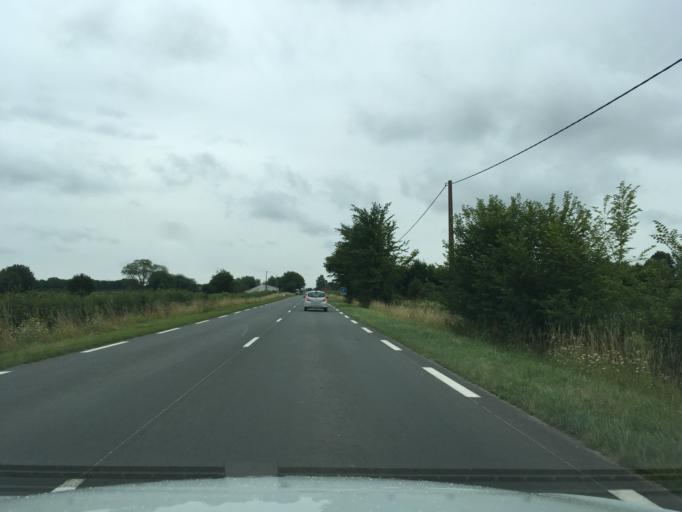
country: FR
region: Picardie
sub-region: Departement de l'Aisne
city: Buironfosse
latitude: 49.9674
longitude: 3.8518
